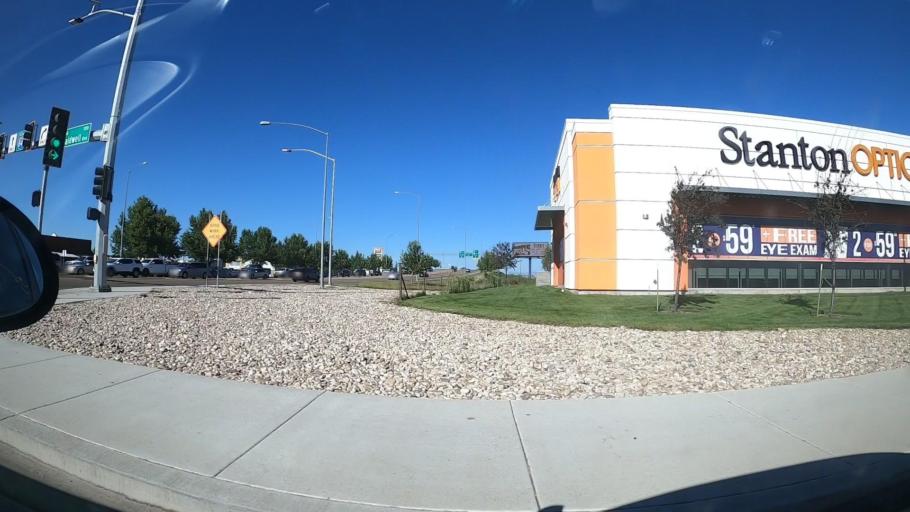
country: US
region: Idaho
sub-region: Canyon County
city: Nampa
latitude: 43.6049
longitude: -116.6021
